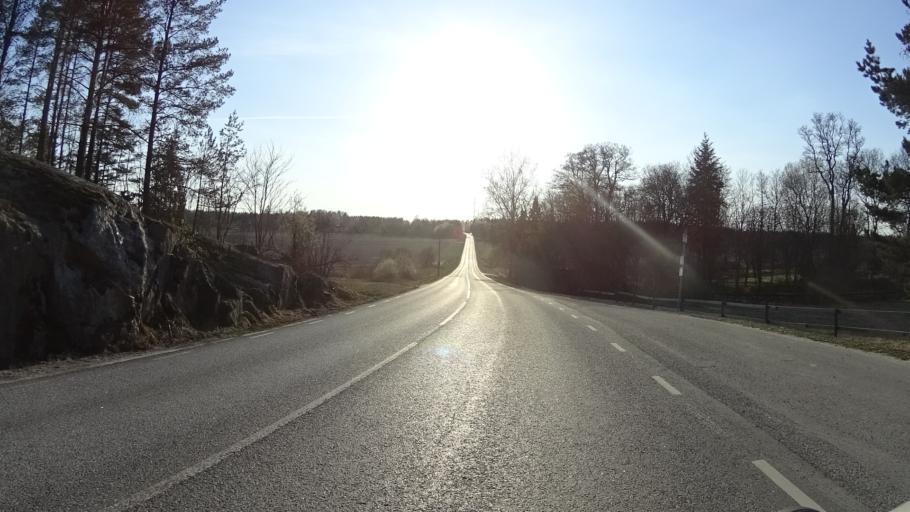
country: SE
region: Stockholm
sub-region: Osterakers Kommun
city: Akersberga
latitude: 59.4507
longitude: 18.2303
